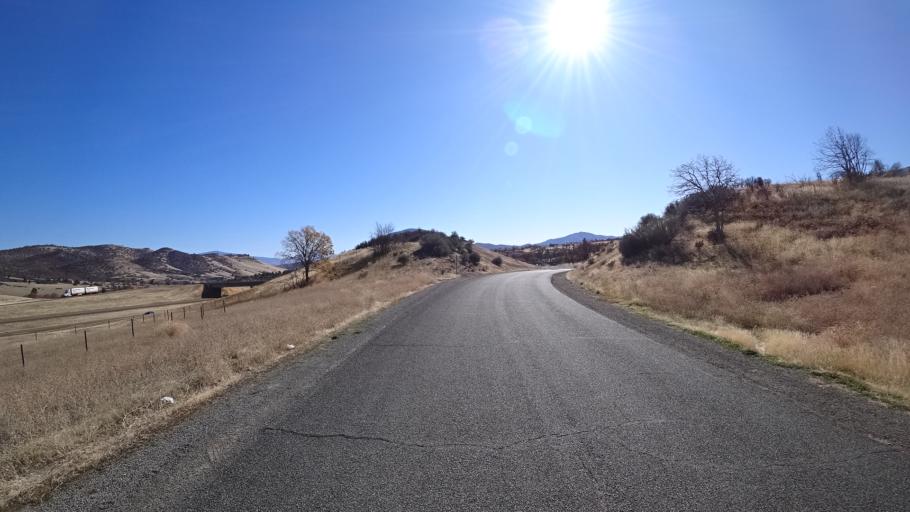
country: US
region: California
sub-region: Siskiyou County
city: Yreka
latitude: 41.9205
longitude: -122.5767
